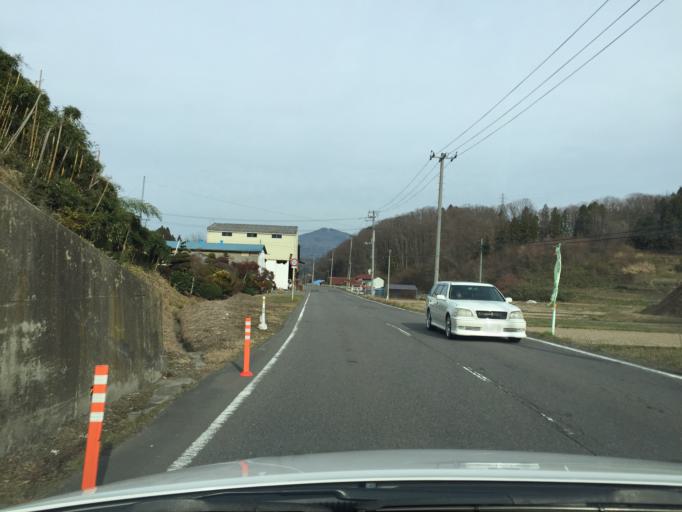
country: JP
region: Fukushima
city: Funehikimachi-funehiki
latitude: 37.4219
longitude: 140.5847
